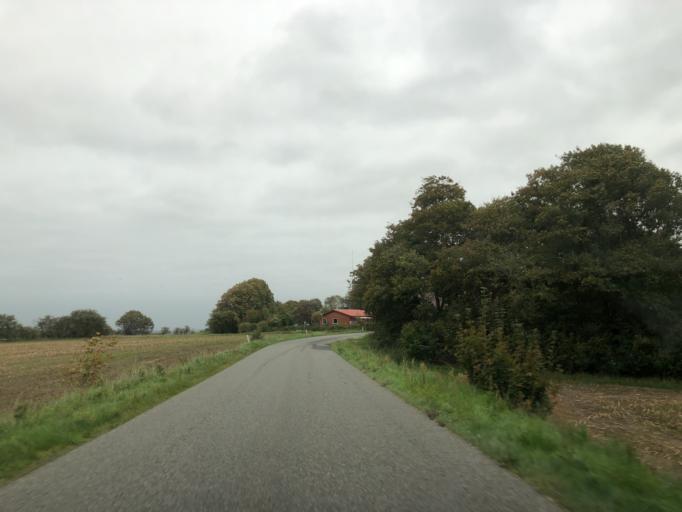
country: DK
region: Central Jutland
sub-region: Viborg Kommune
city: Viborg
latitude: 56.4183
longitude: 9.3095
